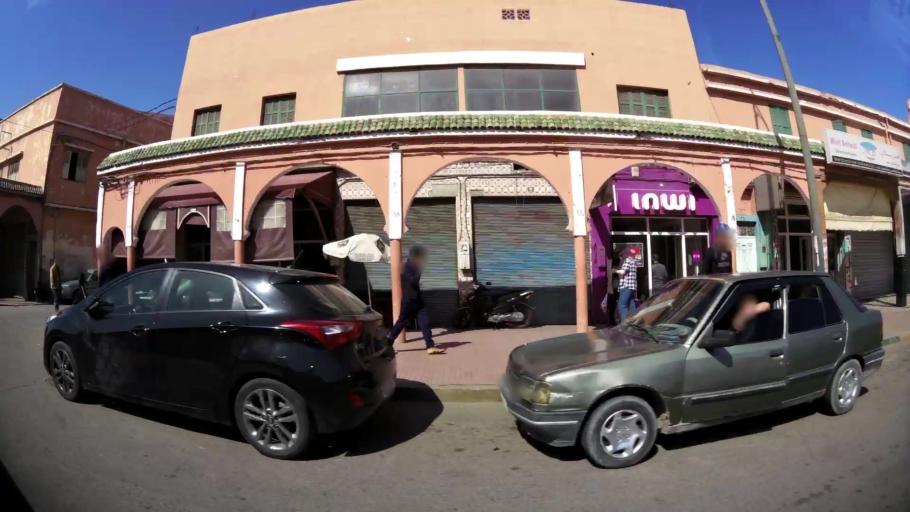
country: MA
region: Souss-Massa-Draa
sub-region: Inezgane-Ait Mellou
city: Inezgane
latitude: 30.3468
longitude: -9.5031
